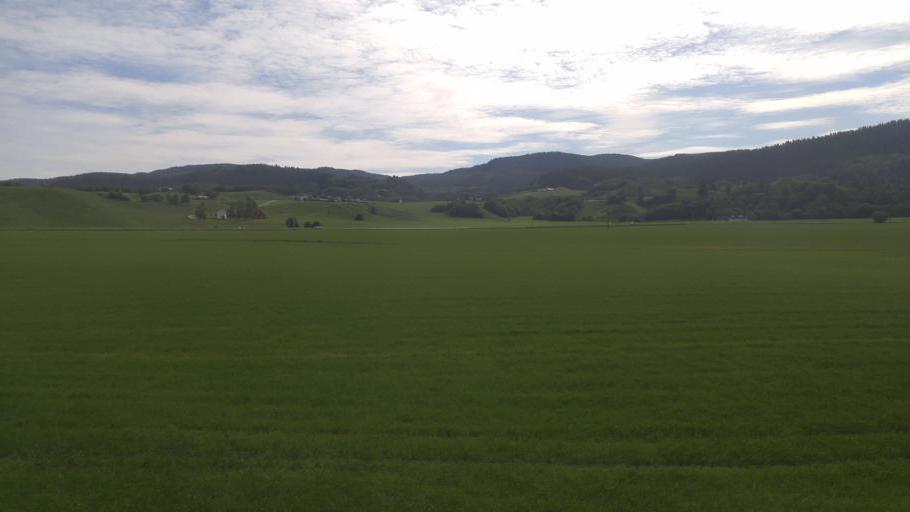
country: NO
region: Sor-Trondelag
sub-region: Melhus
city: Lundamo
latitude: 63.1817
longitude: 10.3081
